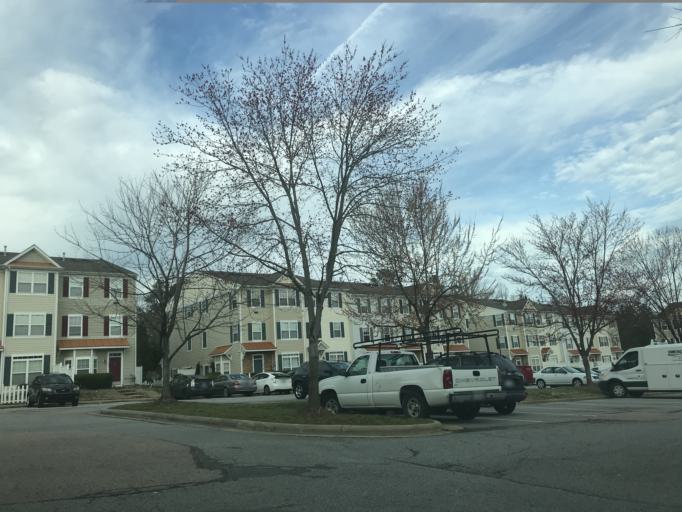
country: US
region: North Carolina
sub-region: Wake County
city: Wake Forest
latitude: 35.9236
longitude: -78.5673
